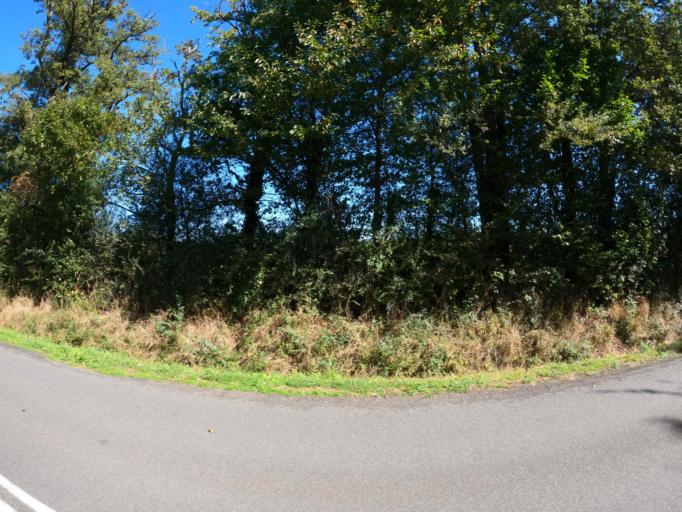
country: FR
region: Limousin
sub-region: Departement de la Haute-Vienne
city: Le Dorat
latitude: 46.2620
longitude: 1.0347
